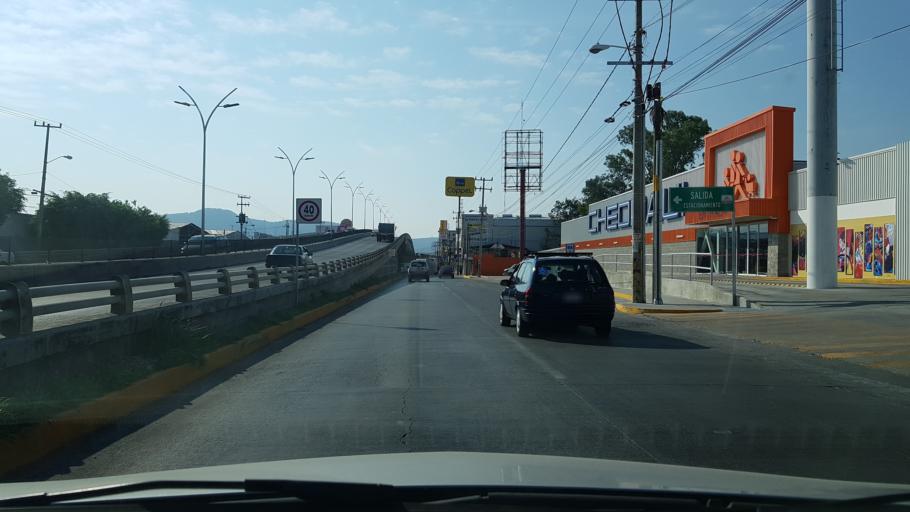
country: MX
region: Morelos
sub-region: Jiutepec
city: Jiutepec
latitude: 18.8989
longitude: -99.1707
